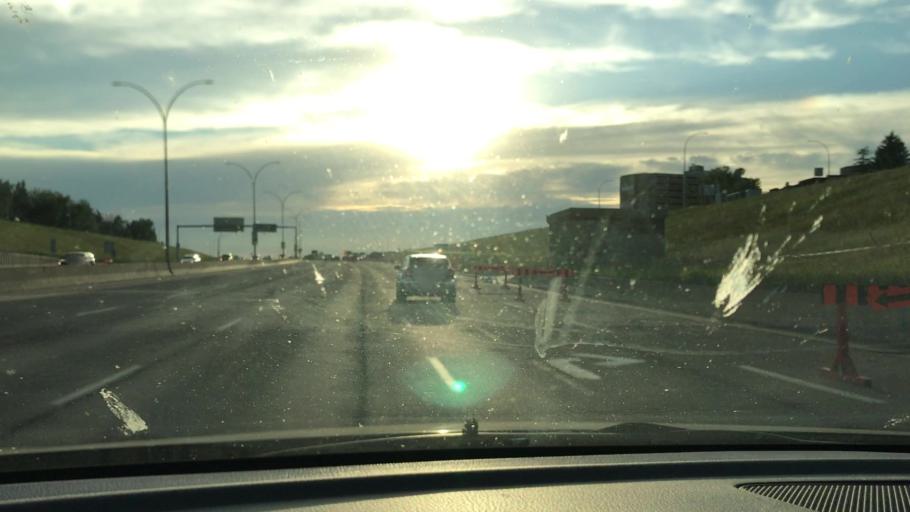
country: CA
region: Alberta
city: Edmonton
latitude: 53.4815
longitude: -113.5050
